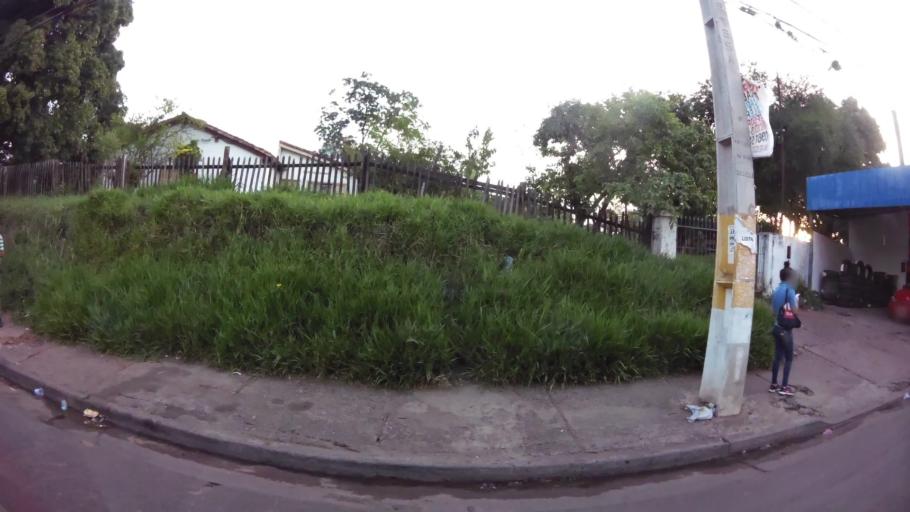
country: PY
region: Central
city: San Lorenzo
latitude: -25.3496
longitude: -57.4943
